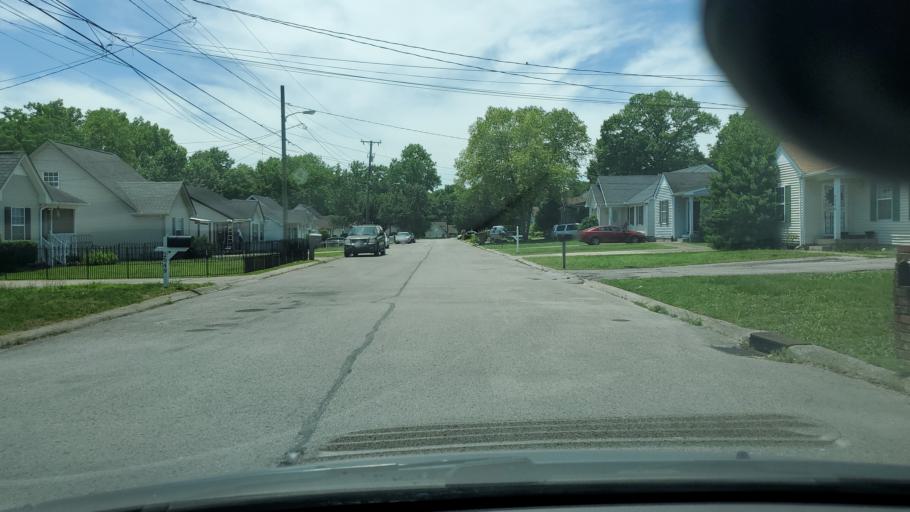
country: US
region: Tennessee
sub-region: Davidson County
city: Nashville
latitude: 36.2113
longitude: -86.7512
